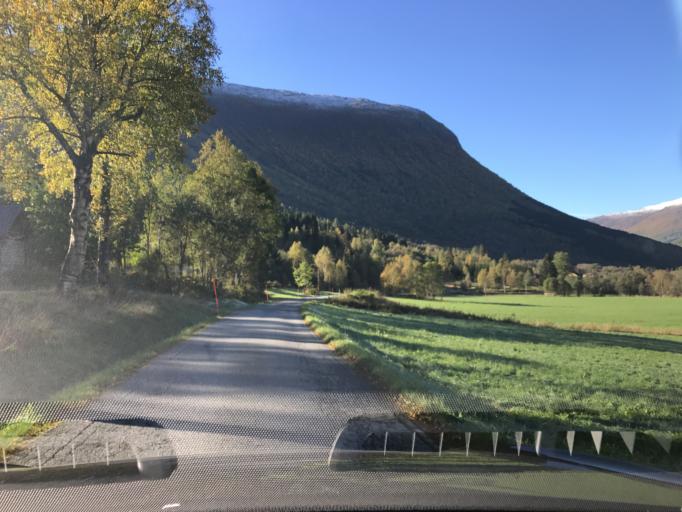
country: NO
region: More og Romsdal
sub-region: Norddal
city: Valldal
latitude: 62.3319
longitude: 7.3889
